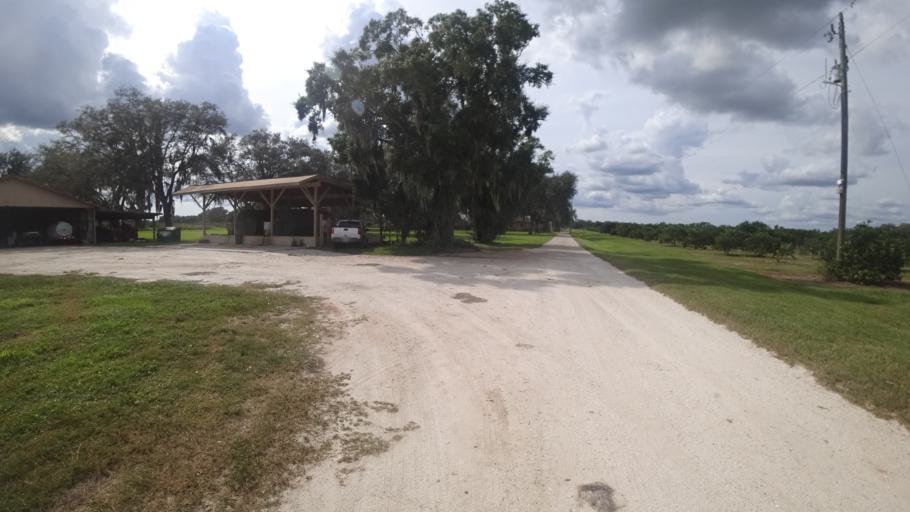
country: US
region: Florida
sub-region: Sarasota County
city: Lake Sarasota
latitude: 27.3429
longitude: -82.2467
